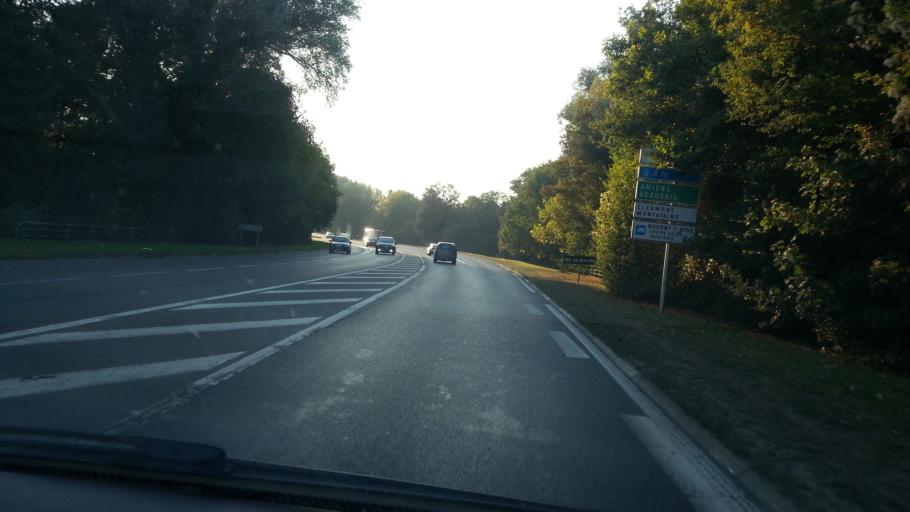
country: FR
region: Picardie
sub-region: Departement de l'Oise
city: Villers-Saint-Paul
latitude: 49.2844
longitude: 2.4840
